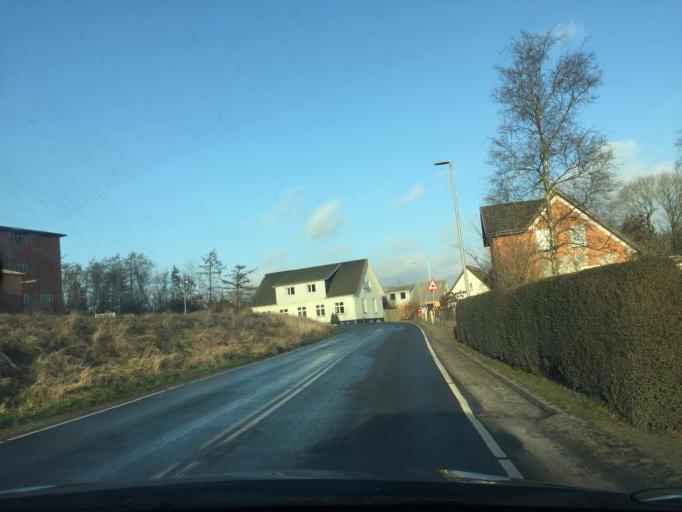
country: DK
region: South Denmark
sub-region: Faaborg-Midtfyn Kommune
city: Ringe
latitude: 55.1913
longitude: 10.3489
